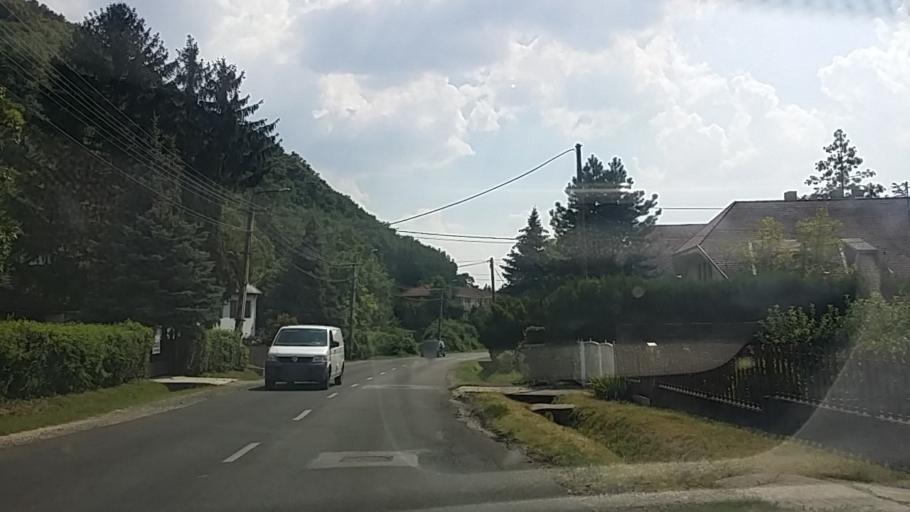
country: HU
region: Baranya
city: Pecs
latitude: 46.0797
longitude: 18.1904
